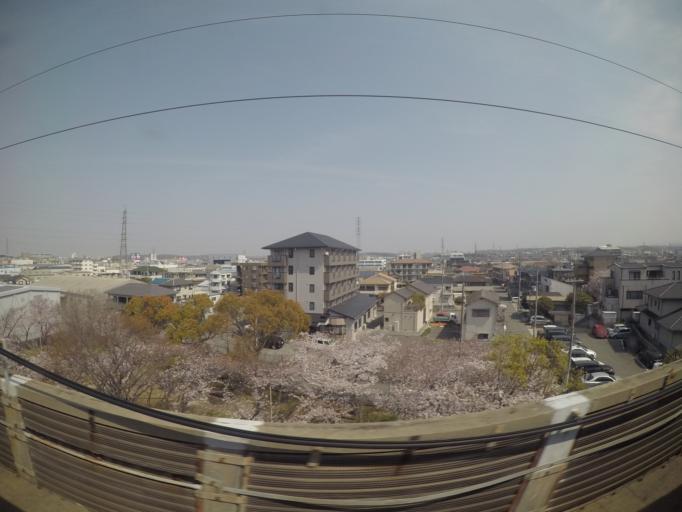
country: JP
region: Hyogo
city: Akashi
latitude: 34.6653
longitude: 134.9847
